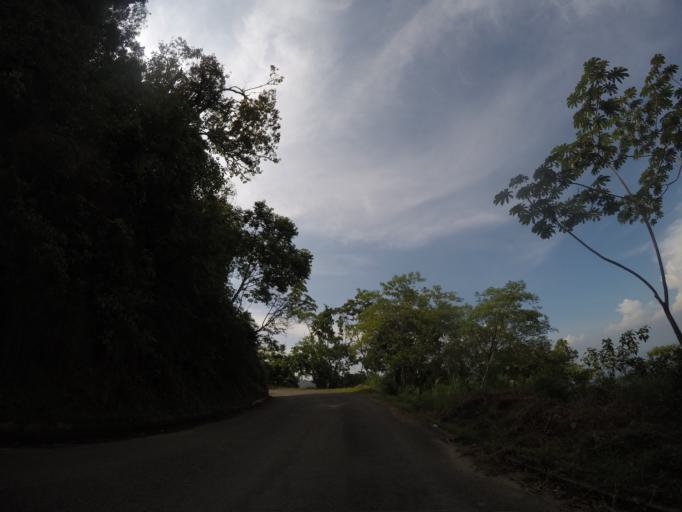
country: MX
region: Oaxaca
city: Pluma Hidalgo
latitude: 15.9416
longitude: -96.4422
